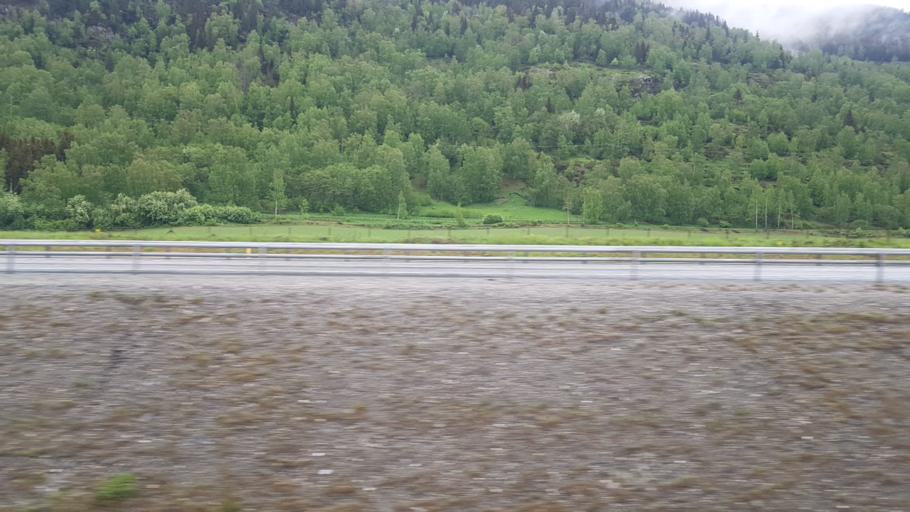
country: NO
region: Oppland
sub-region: Sor-Fron
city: Hundorp
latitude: 61.5474
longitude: 10.0305
